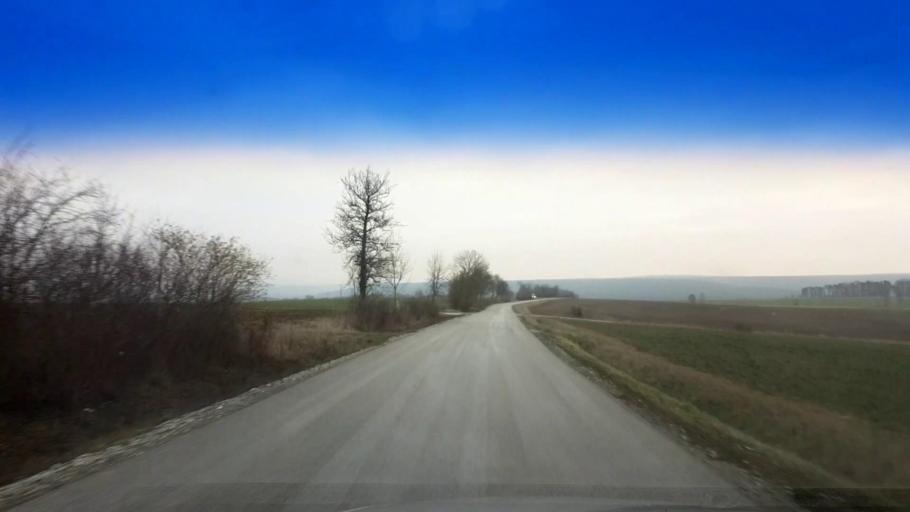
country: DE
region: Bavaria
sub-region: Upper Franconia
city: Hallerndorf
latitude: 49.7779
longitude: 10.9832
